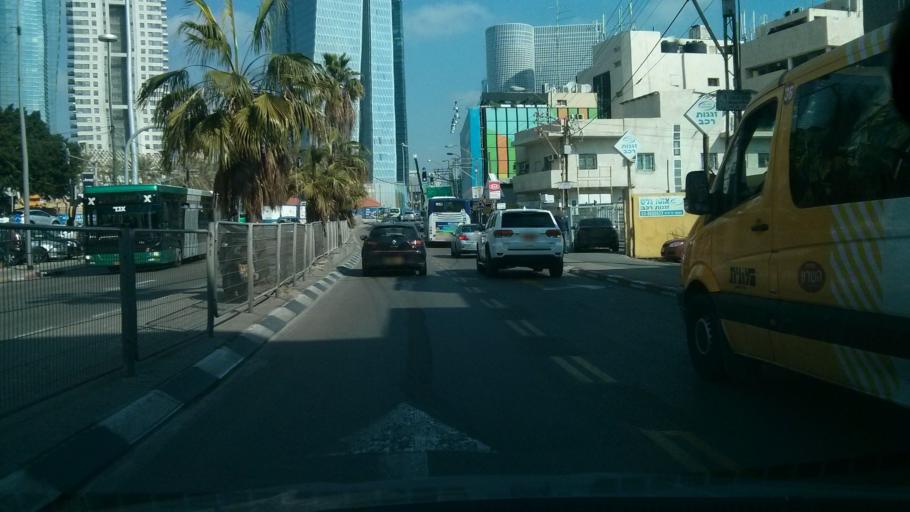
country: IL
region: Tel Aviv
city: Tel Aviv
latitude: 32.0682
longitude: 34.7874
